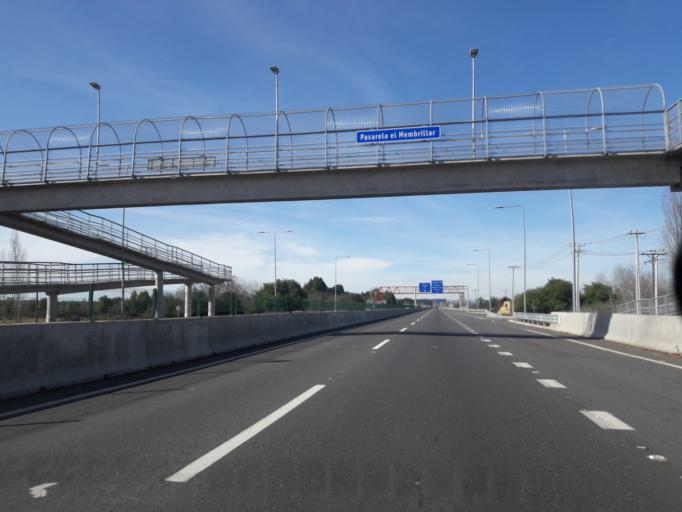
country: CL
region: Biobio
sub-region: Provincia de Biobio
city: Cabrero
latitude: -37.0271
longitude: -72.4468
